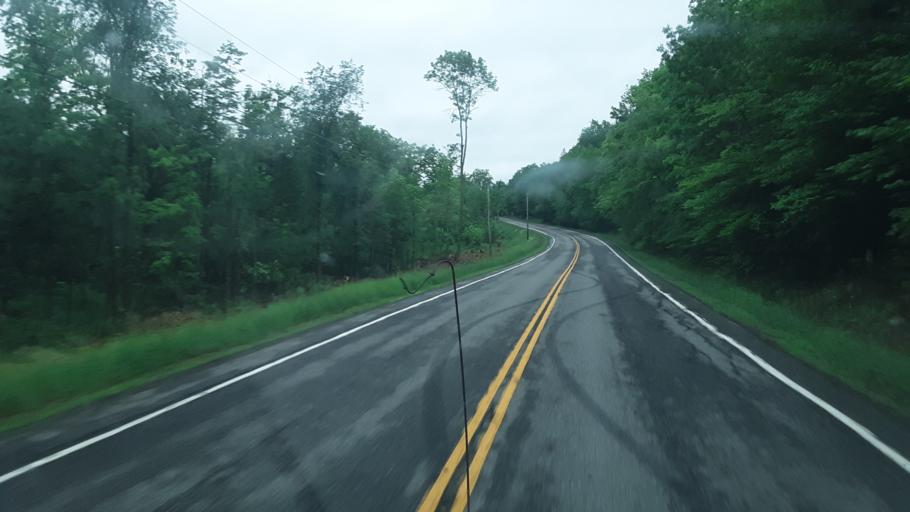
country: US
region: Maine
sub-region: Penobscot County
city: Patten
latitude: 46.1601
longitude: -68.3480
